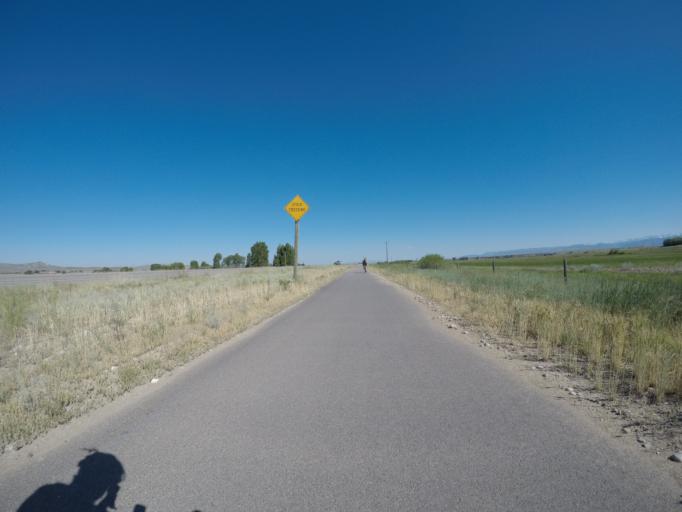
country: US
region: Wyoming
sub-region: Sublette County
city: Pinedale
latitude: 42.8218
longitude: -109.8414
